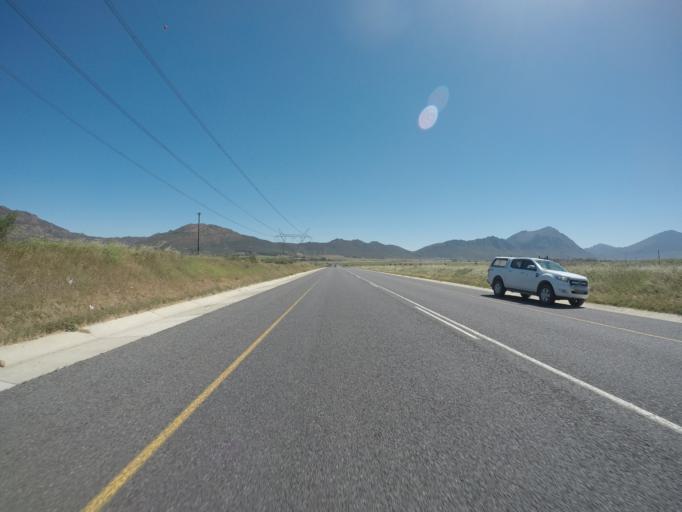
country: ZA
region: Western Cape
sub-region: Cape Winelands District Municipality
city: Ceres
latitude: -33.3116
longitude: 19.1202
